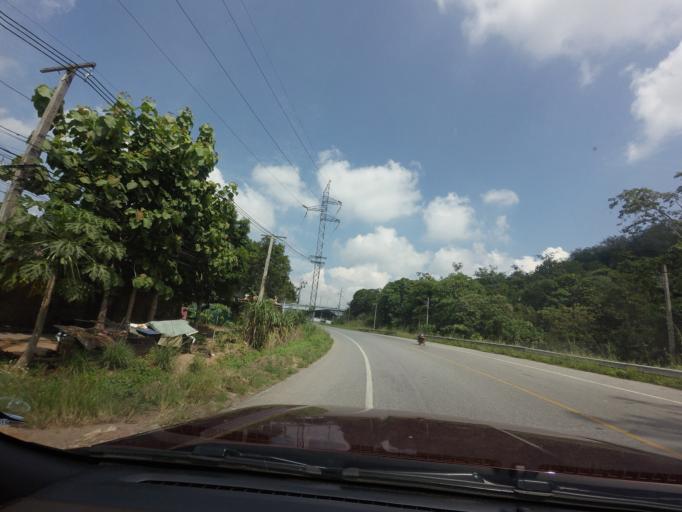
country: TH
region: Yala
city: Betong
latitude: 5.8225
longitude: 101.1081
